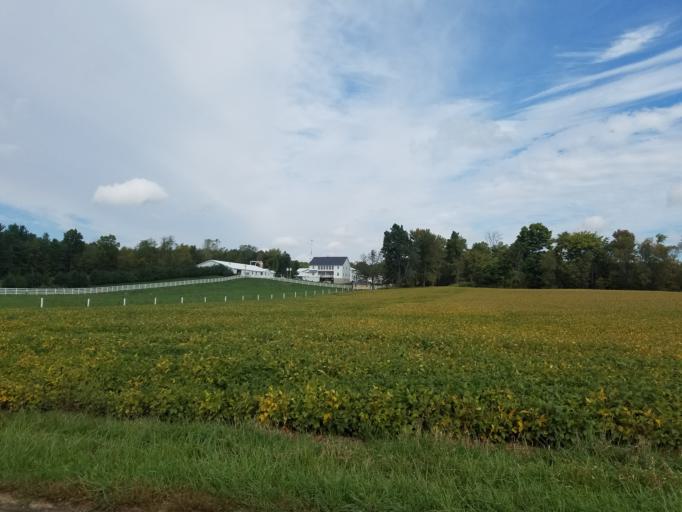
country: US
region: Ohio
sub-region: Knox County
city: Fredericktown
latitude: 40.5207
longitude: -82.6667
